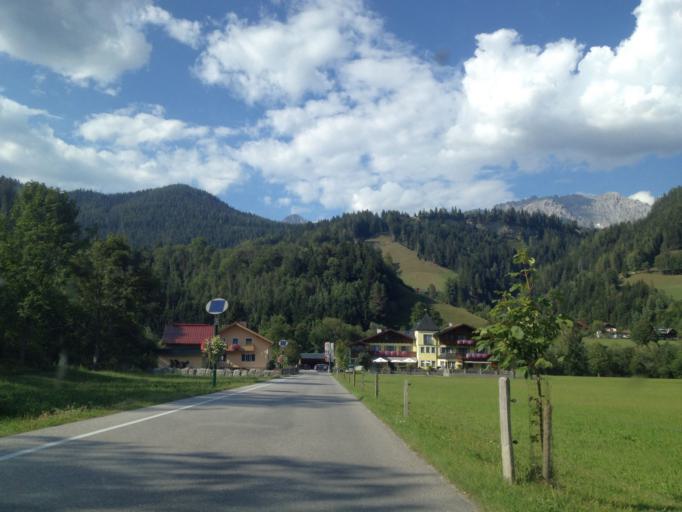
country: AT
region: Styria
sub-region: Politischer Bezirk Liezen
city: Schladming
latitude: 47.3864
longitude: 13.6175
